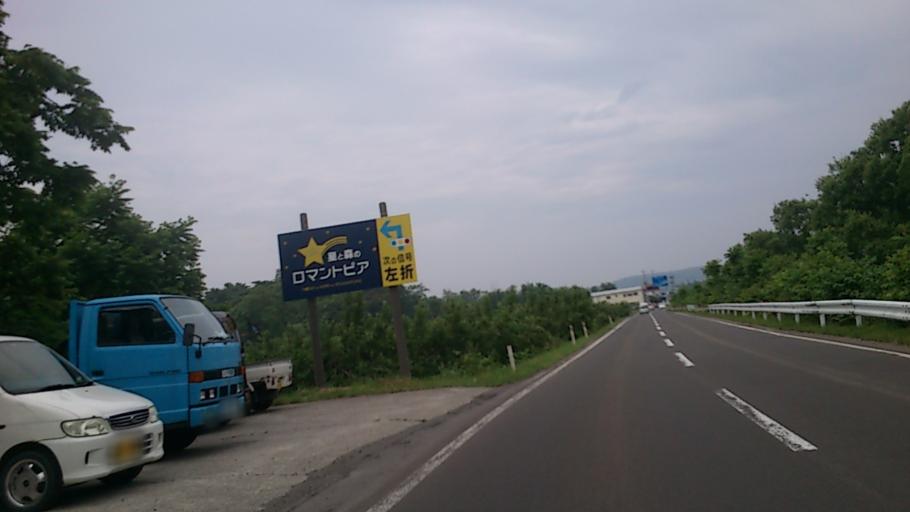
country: JP
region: Aomori
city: Hirosaki
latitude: 40.5925
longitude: 140.4205
